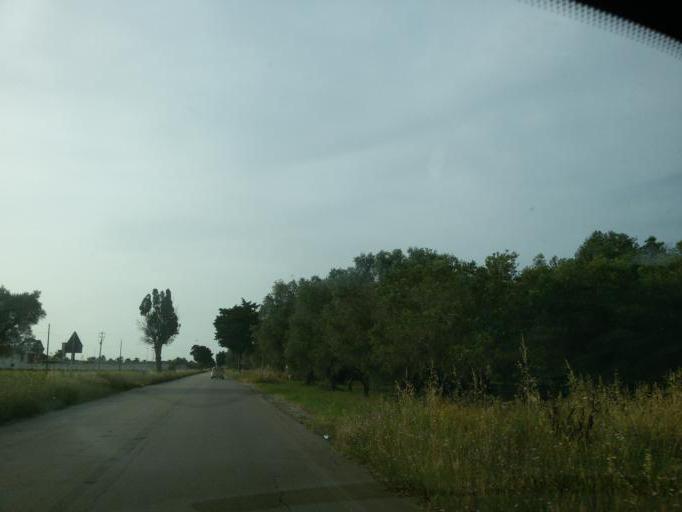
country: IT
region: Apulia
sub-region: Provincia di Brindisi
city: San Pietro Vernotico
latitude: 40.5185
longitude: 17.9870
